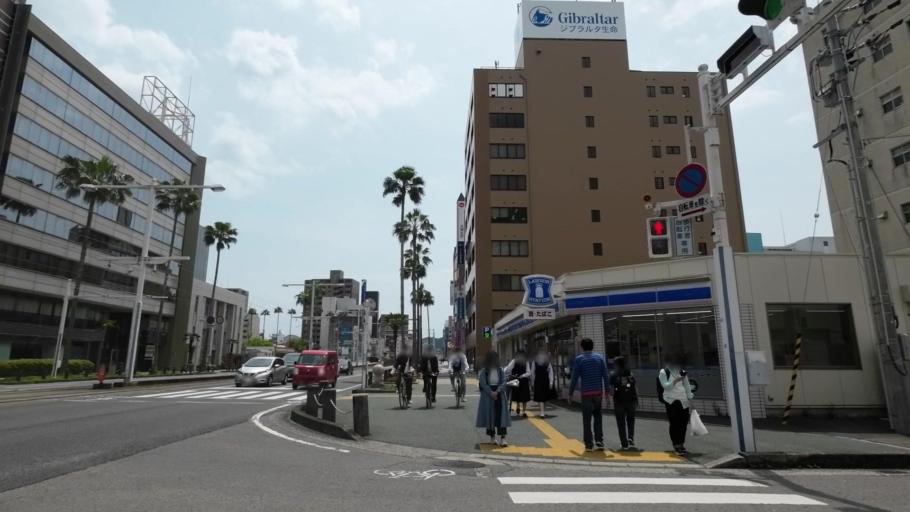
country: JP
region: Kochi
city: Kochi-shi
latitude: 33.5655
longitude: 133.5434
